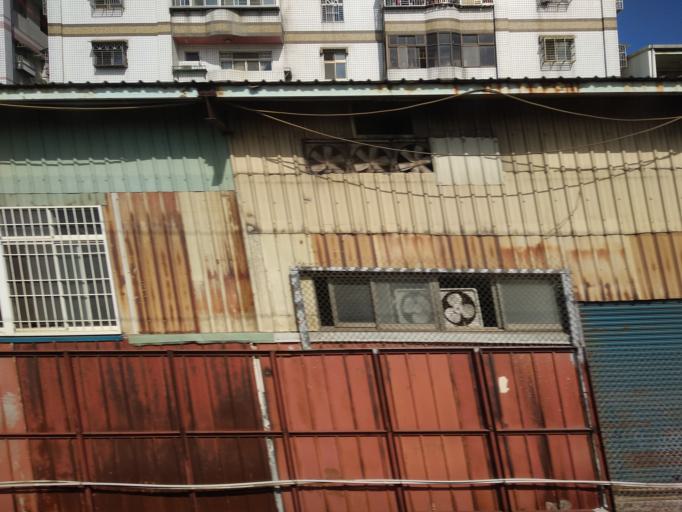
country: TW
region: Taiwan
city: Taoyuan City
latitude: 24.9841
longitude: 121.2907
